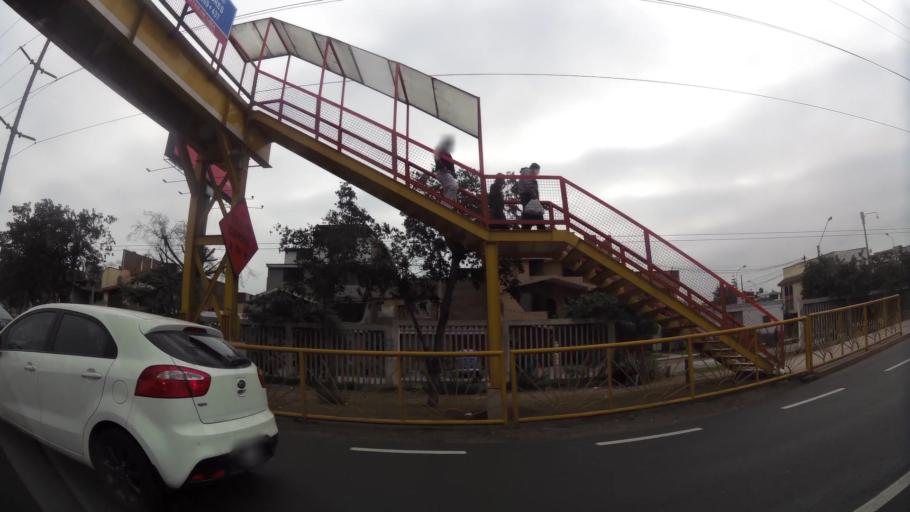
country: PE
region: Lima
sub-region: Lima
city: Surco
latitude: -12.1412
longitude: -76.9813
